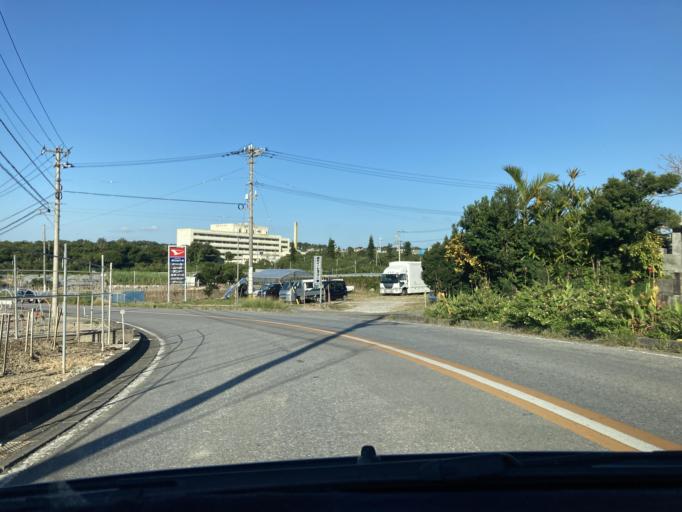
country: JP
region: Okinawa
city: Itoman
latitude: 26.1091
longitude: 127.6679
